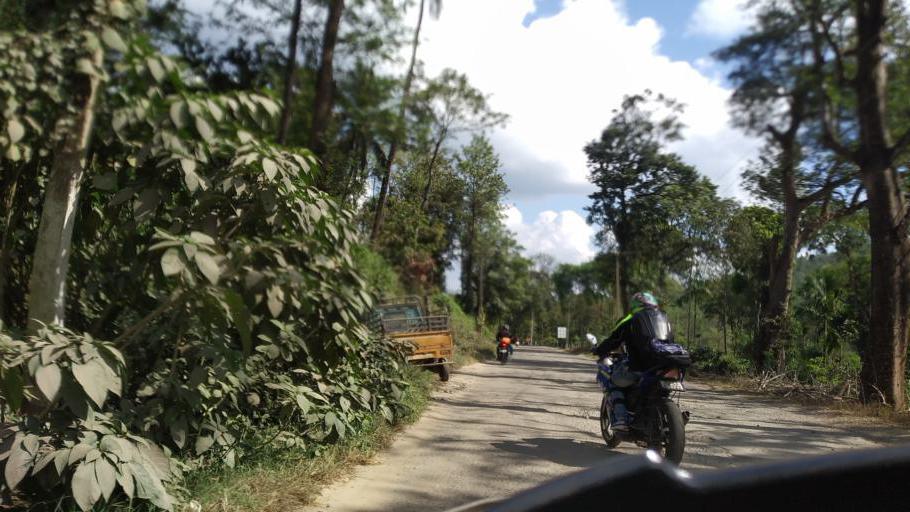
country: IN
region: Karnataka
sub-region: Kodagu
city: Ponnampet
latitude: 11.9659
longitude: 76.0547
